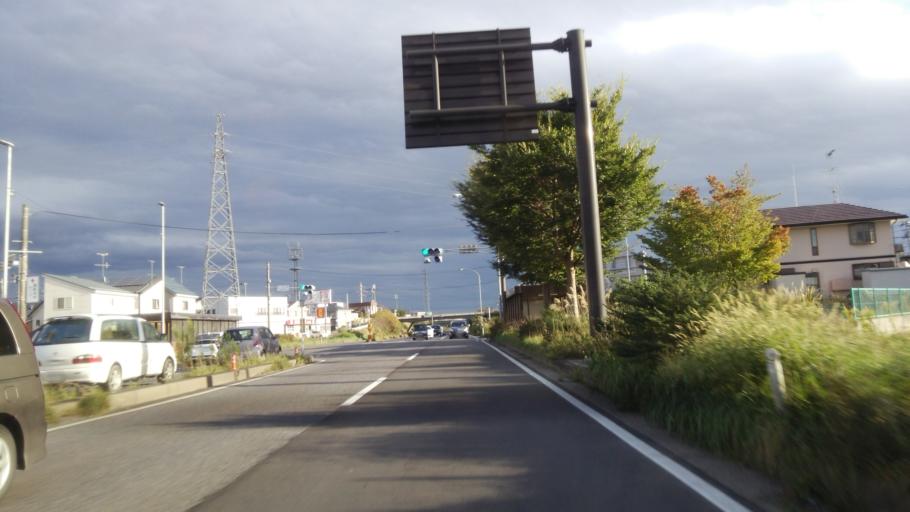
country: JP
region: Fukushima
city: Koriyama
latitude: 37.3810
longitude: 140.3462
